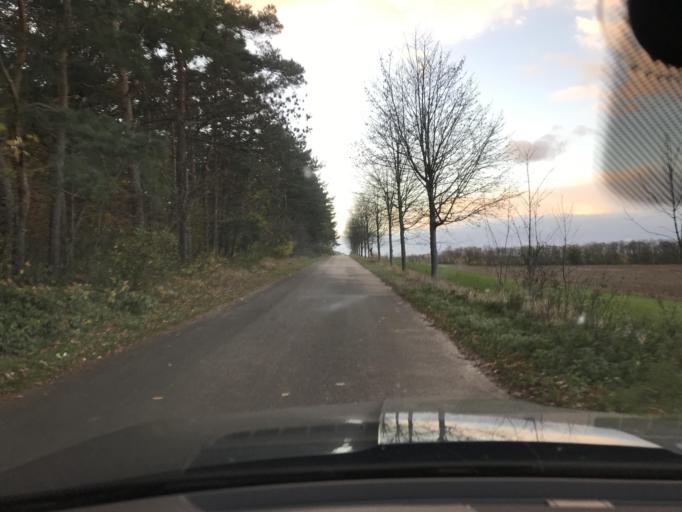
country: DE
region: Saxony-Anhalt
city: Langenstein
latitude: 51.8446
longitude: 11.0218
